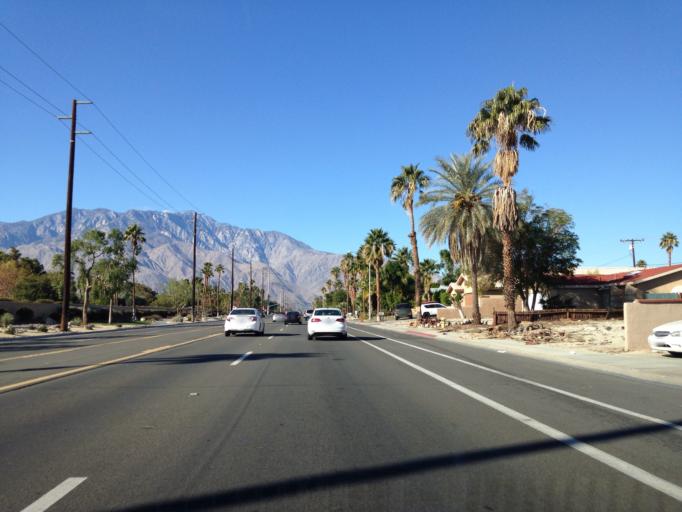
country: US
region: California
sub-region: Riverside County
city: Palm Springs
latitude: 33.8449
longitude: -116.4802
